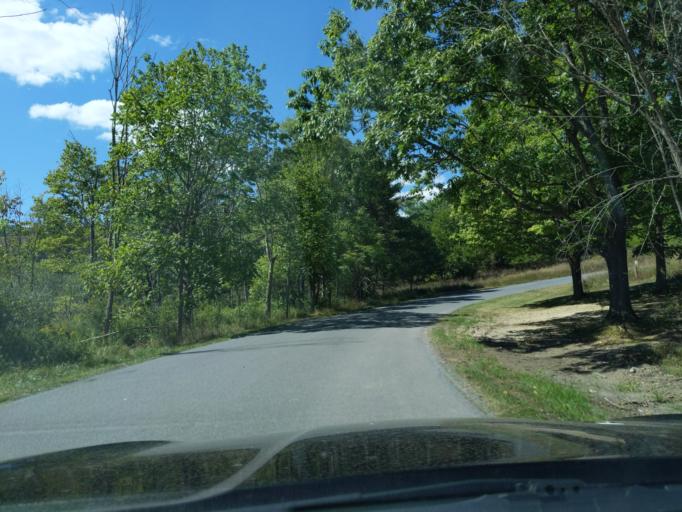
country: US
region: Pennsylvania
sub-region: Blair County
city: Greenwood
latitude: 40.4809
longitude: -78.2935
